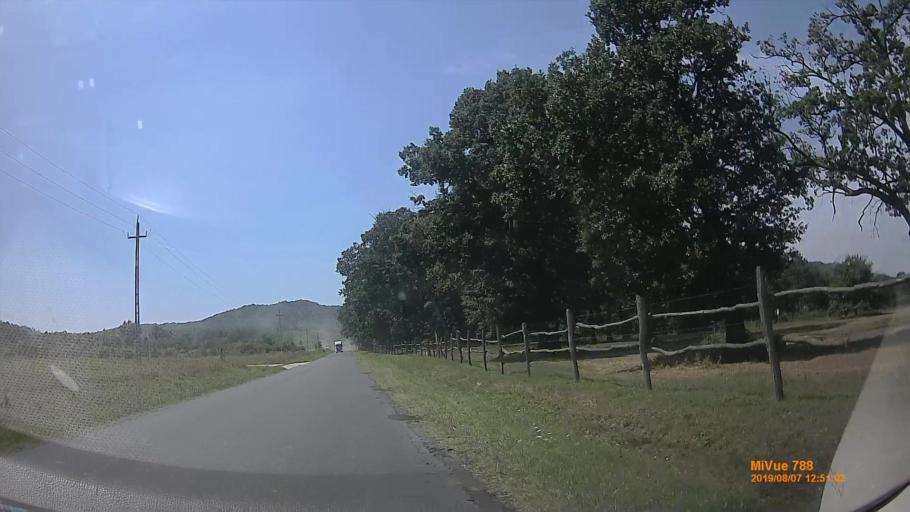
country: HU
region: Zala
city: Cserszegtomaj
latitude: 46.8616
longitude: 17.2763
